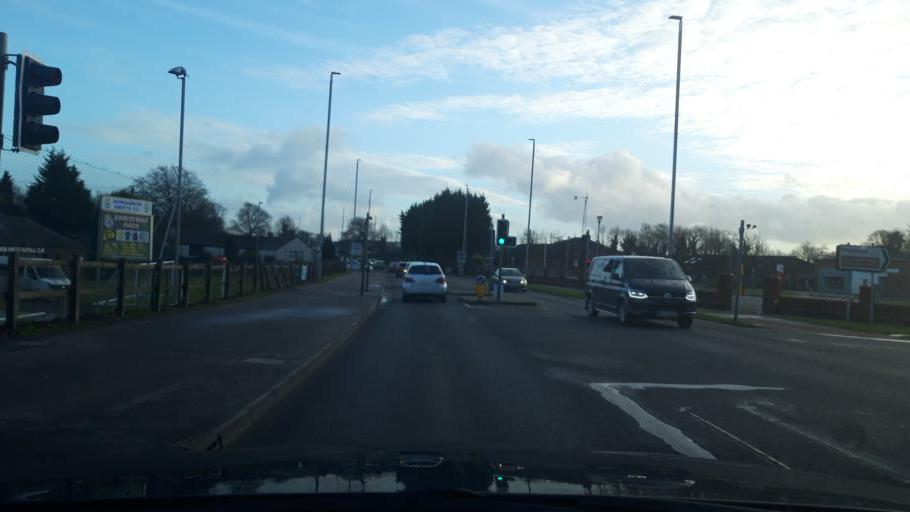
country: GB
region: Northern Ireland
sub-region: Dungannon District
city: Dungannon
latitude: 54.4891
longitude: -6.7476
